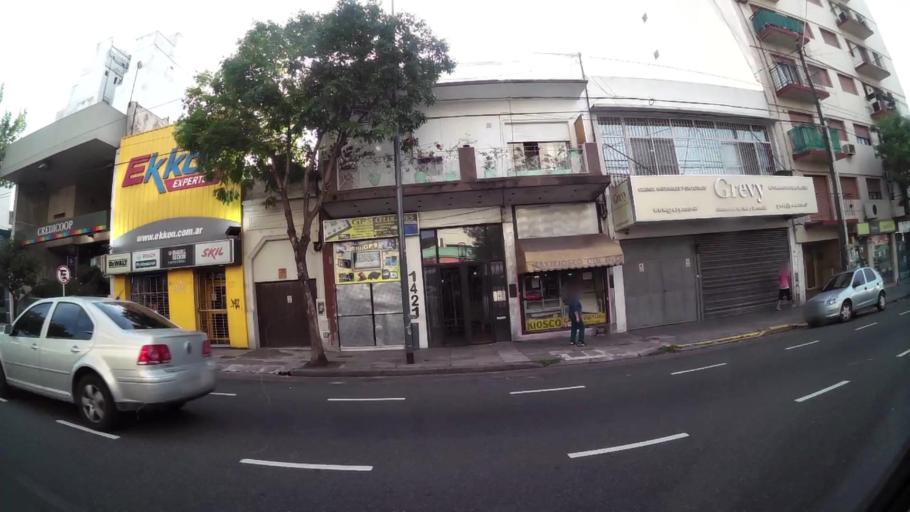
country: AR
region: Buenos Aires F.D.
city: Buenos Aires
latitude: -34.6318
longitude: -58.4257
